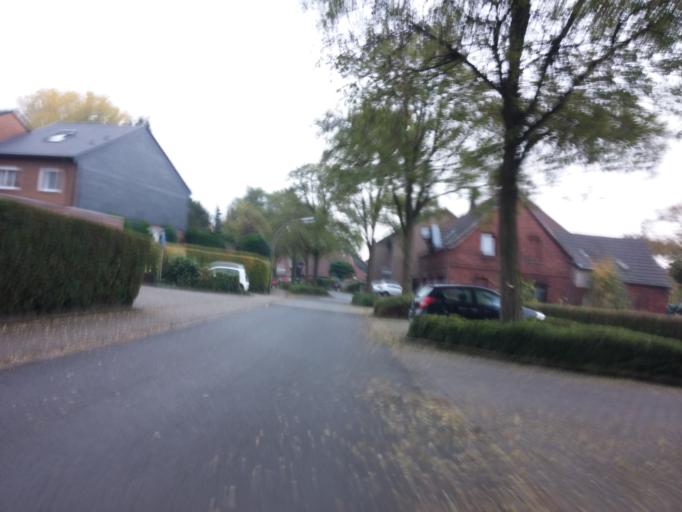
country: DE
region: North Rhine-Westphalia
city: Dorsten
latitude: 51.6622
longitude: 6.9457
